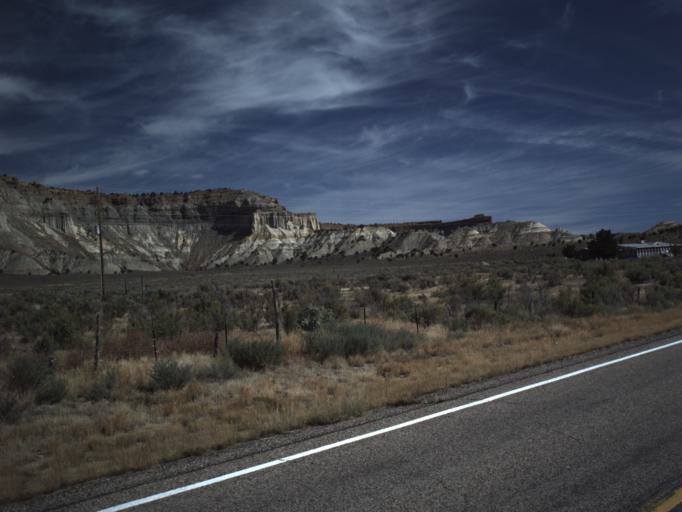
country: US
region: Utah
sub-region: Garfield County
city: Panguitch
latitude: 37.5621
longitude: -112.0128
